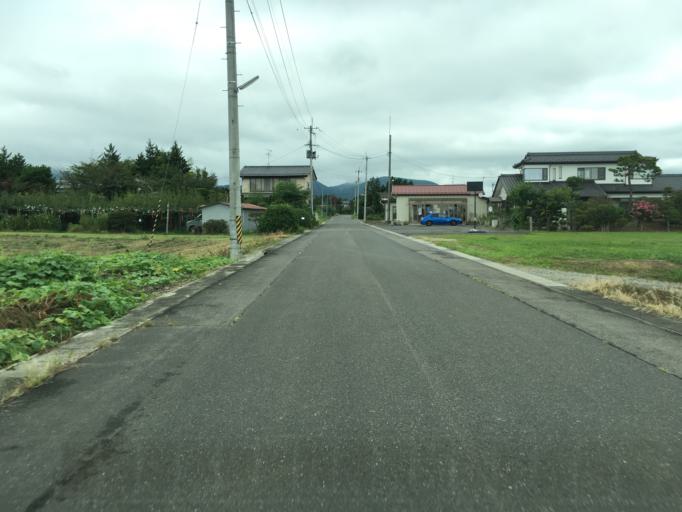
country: JP
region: Fukushima
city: Fukushima-shi
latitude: 37.7726
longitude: 140.4064
